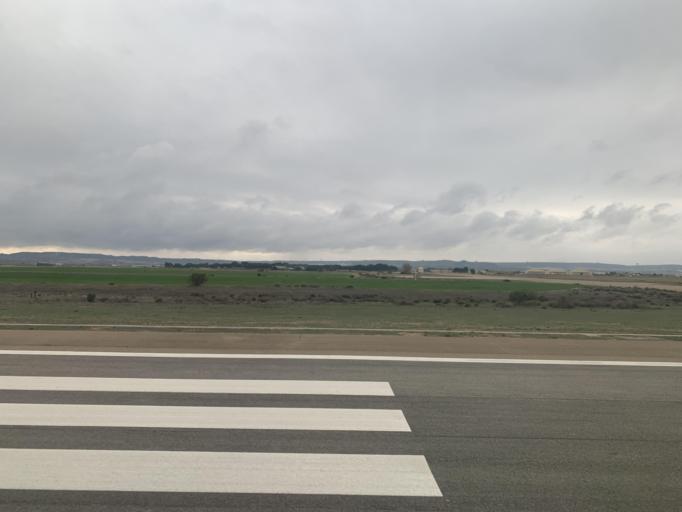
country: ES
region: Aragon
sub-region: Provincia de Zaragoza
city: Utebo
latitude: 41.6684
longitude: -1.0383
